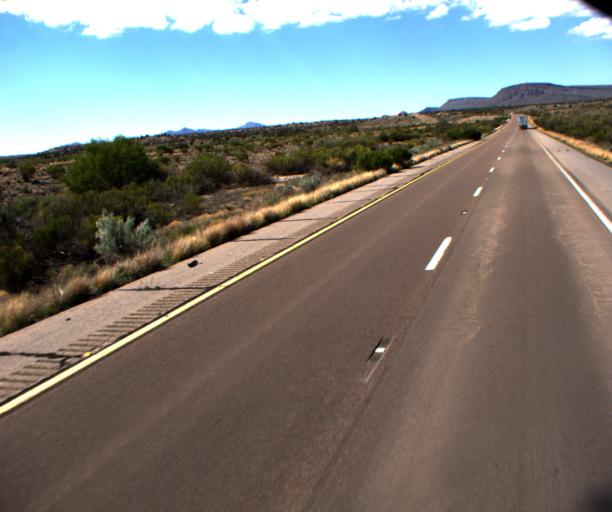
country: US
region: Arizona
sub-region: Mohave County
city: Kingman
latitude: 35.1205
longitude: -113.6662
